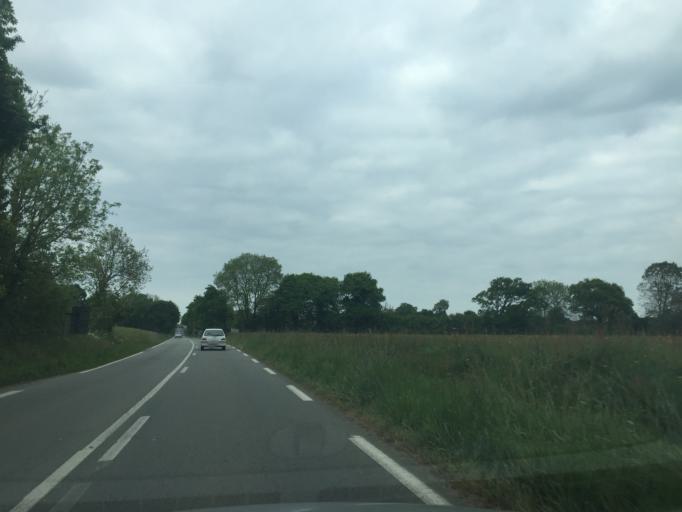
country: FR
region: Brittany
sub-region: Departement des Cotes-d'Armor
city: Saint-Cast-le-Guildo
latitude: 48.6114
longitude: -2.2725
